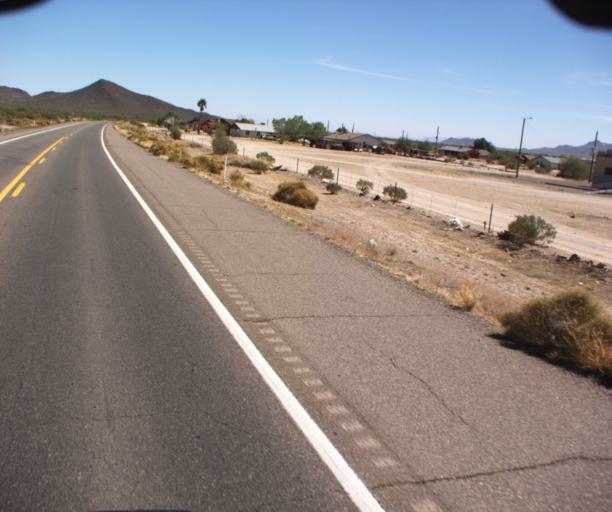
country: US
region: Arizona
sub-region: Pinal County
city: Sacaton
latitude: 33.1210
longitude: -111.7367
